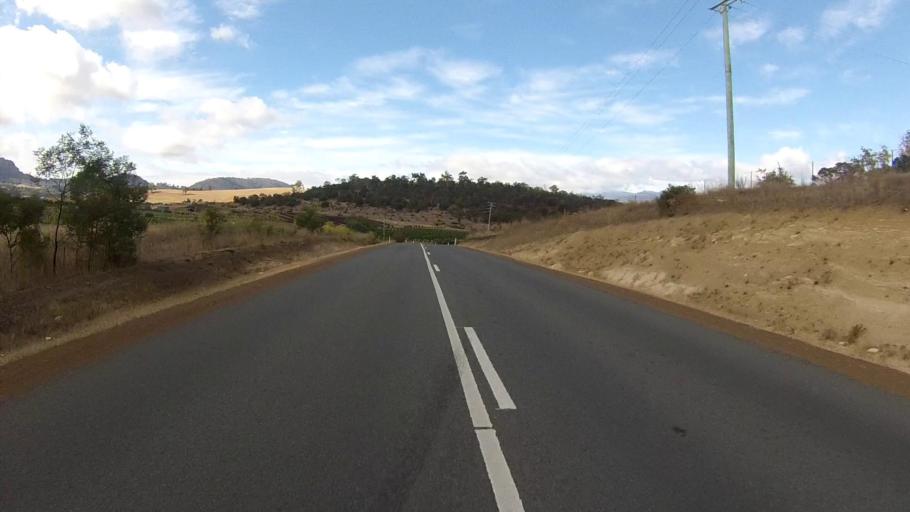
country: AU
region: Tasmania
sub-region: Brighton
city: Old Beach
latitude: -42.7393
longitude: 147.2881
